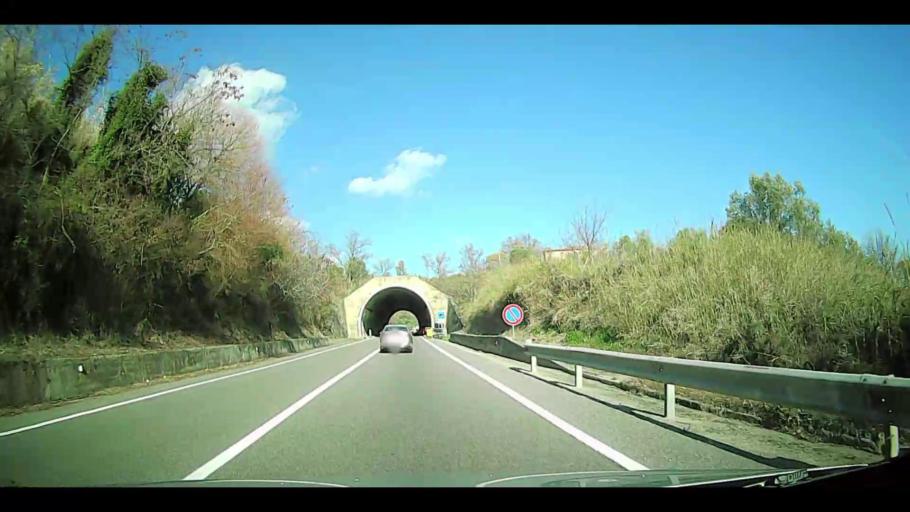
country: IT
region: Calabria
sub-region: Provincia di Crotone
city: Caccuri
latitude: 39.2187
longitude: 16.7955
